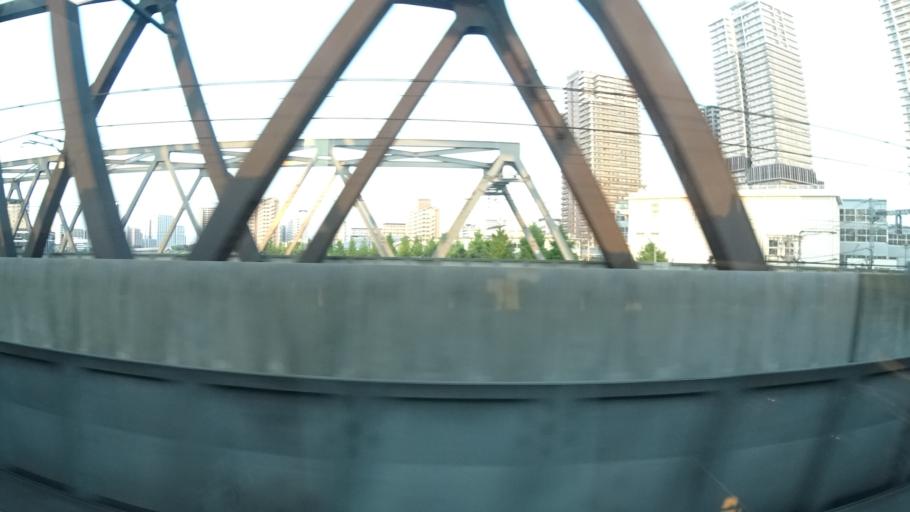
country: JP
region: Saitama
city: Soka
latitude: 35.7383
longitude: 139.8011
